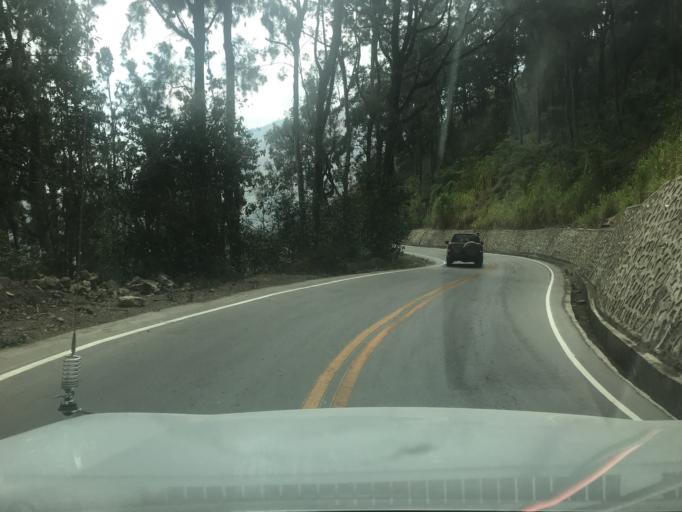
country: TL
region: Manufahi
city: Same
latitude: -8.8906
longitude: 125.5949
